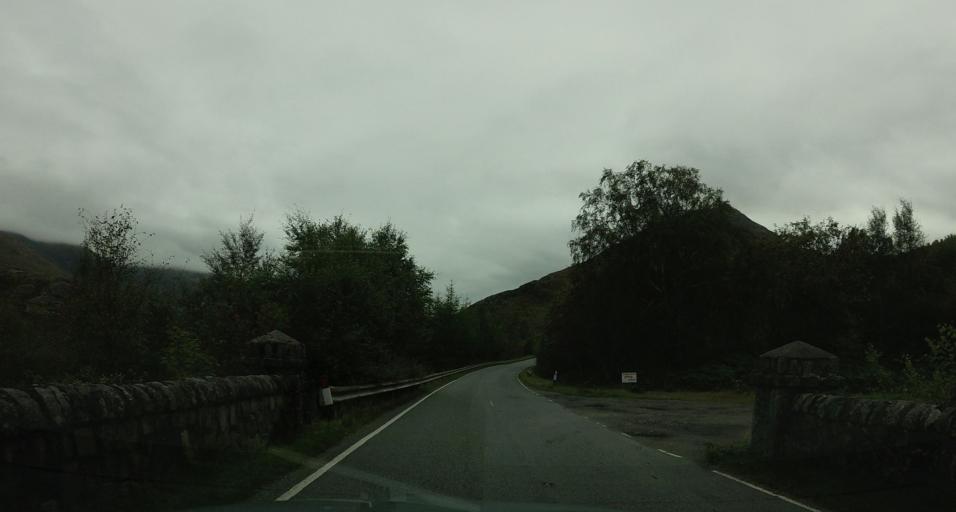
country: GB
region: Scotland
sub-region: Highland
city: Fort William
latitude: 56.7014
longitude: -5.0388
